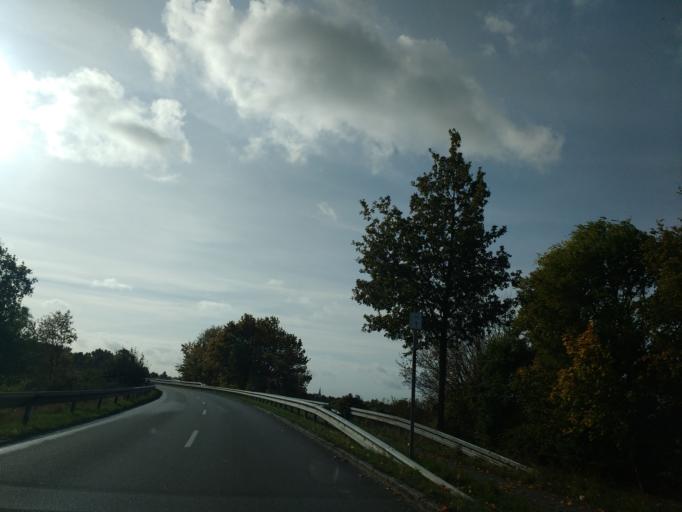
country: DE
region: Schleswig-Holstein
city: Altenkrempe
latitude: 54.1280
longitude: 10.8213
